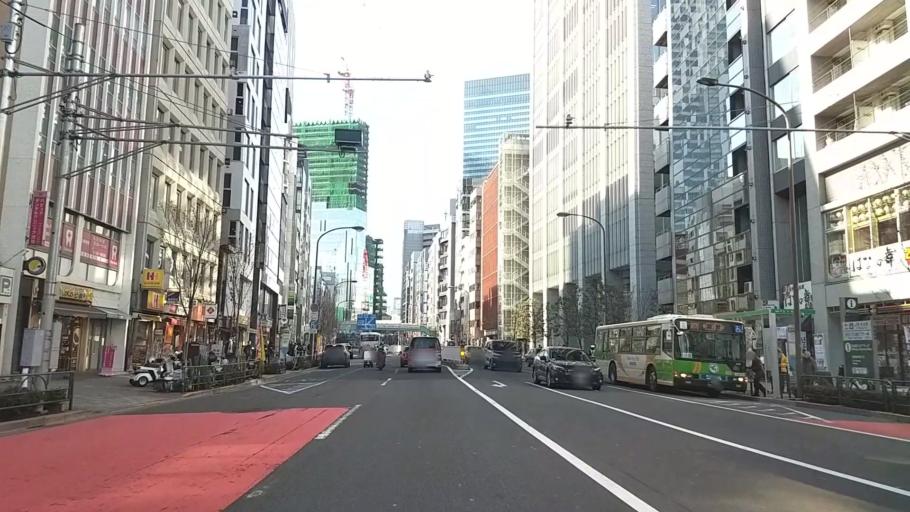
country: JP
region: Tokyo
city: Tokyo
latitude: 35.6554
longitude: 139.7064
